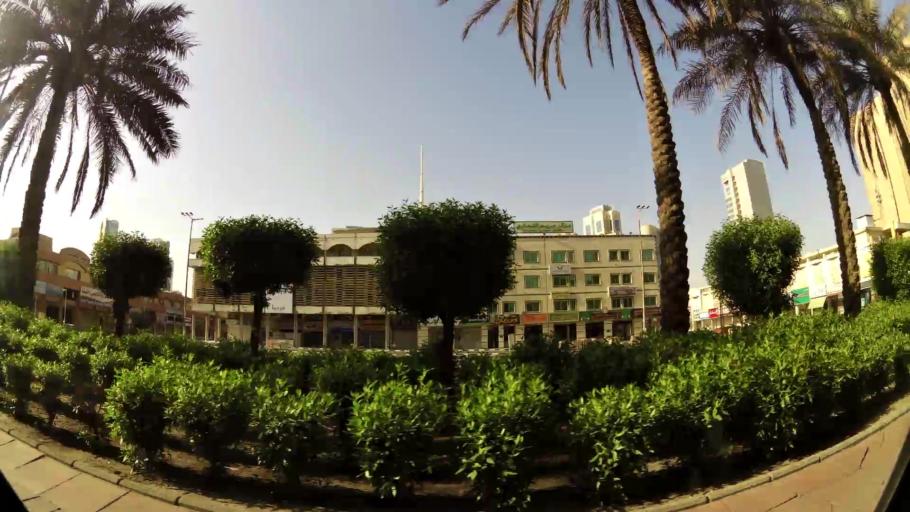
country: KW
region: Al Asimah
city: Kuwait City
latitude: 29.3740
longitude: 47.9798
